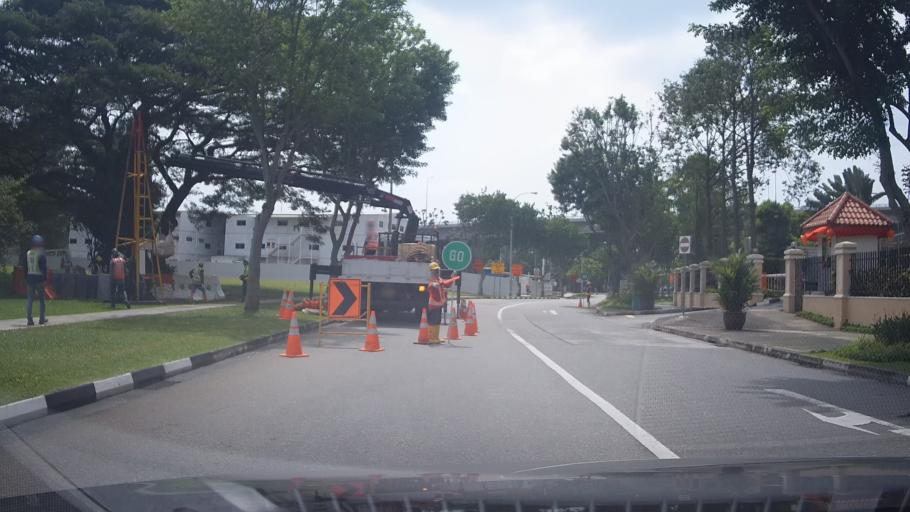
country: SG
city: Singapore
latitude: 1.2965
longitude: 103.8679
